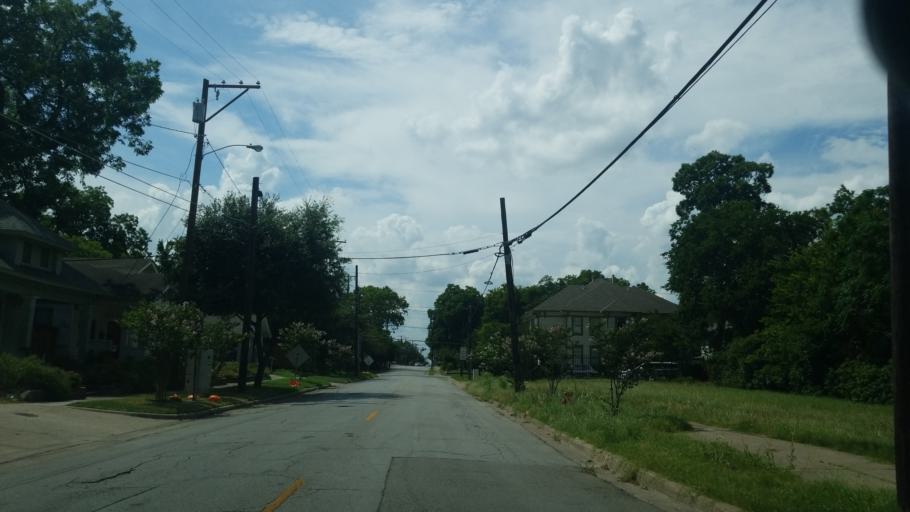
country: US
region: Texas
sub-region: Dallas County
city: Dallas
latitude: 32.7952
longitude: -96.7717
